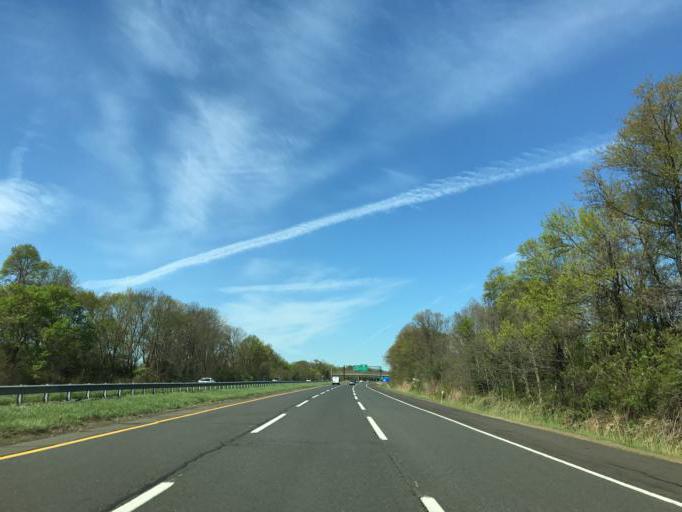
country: US
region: New Jersey
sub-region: Burlington County
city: Roebling
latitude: 40.0945
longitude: -74.7622
